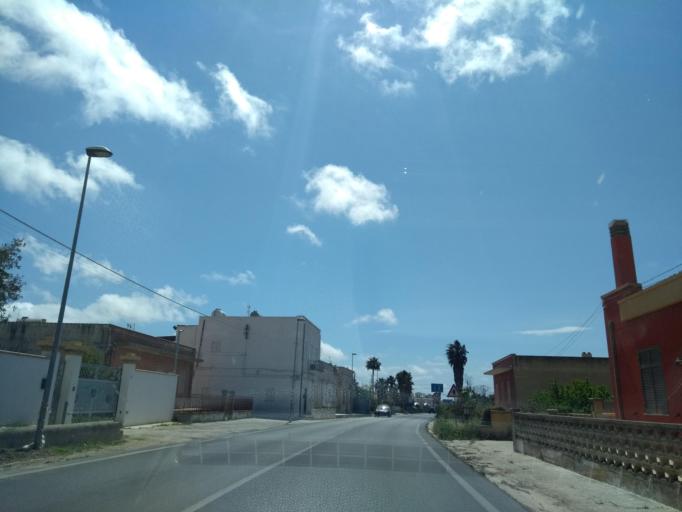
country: IT
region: Sicily
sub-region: Trapani
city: Marsala
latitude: 37.8527
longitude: 12.5133
